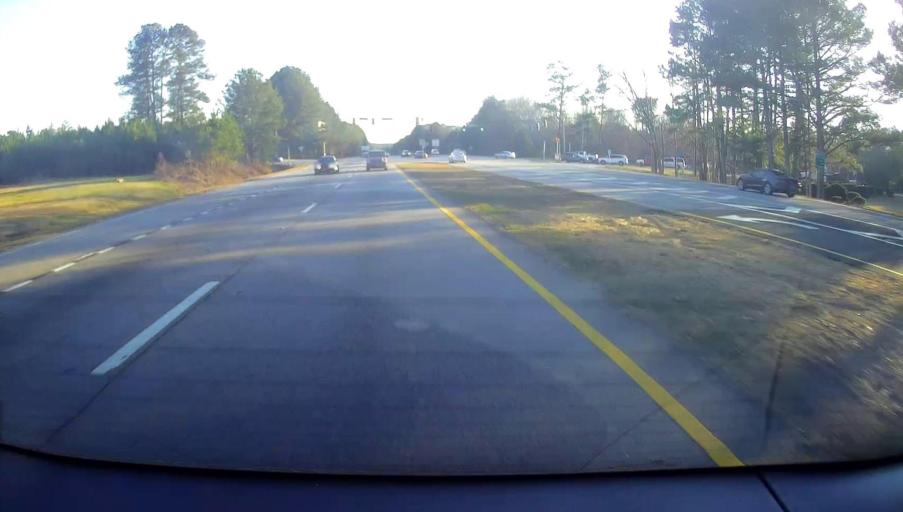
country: US
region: Georgia
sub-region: Fayette County
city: Tyrone
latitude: 33.4797
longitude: -84.5857
